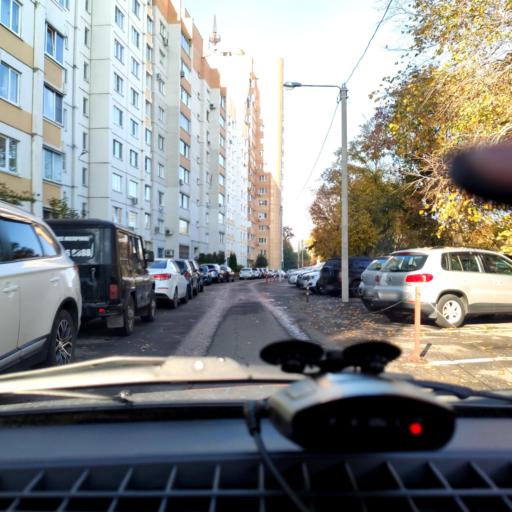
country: RU
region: Voronezj
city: Voronezh
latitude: 51.7045
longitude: 39.2228
